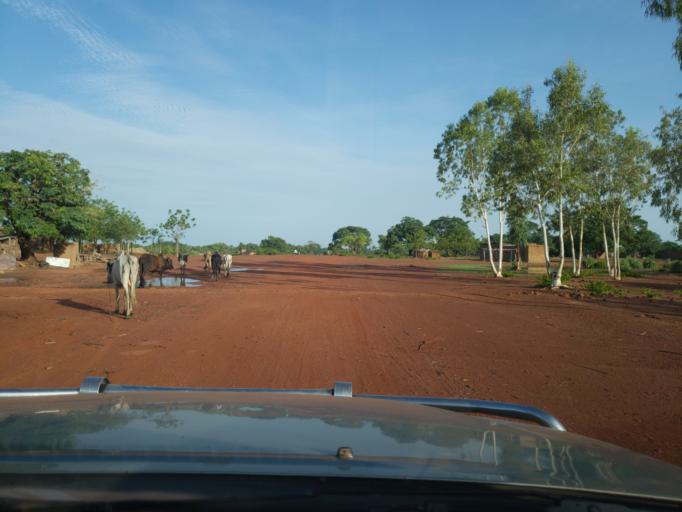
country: ML
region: Sikasso
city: Koutiala
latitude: 12.4191
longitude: -5.5783
